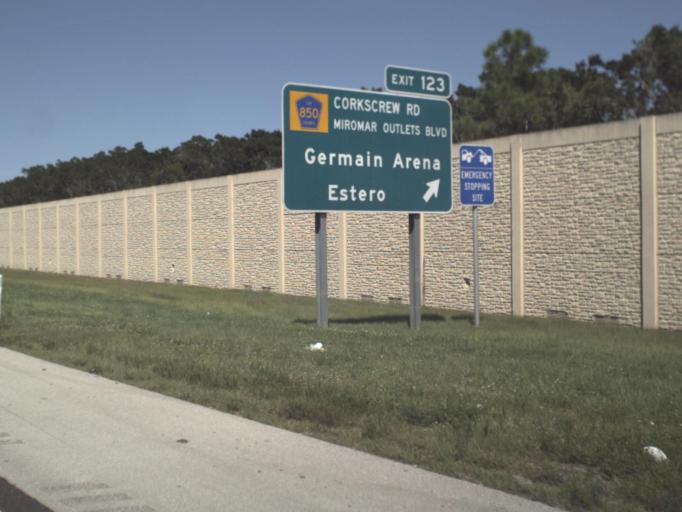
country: US
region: Florida
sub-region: Lee County
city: Estero
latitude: 26.4271
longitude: -81.7757
